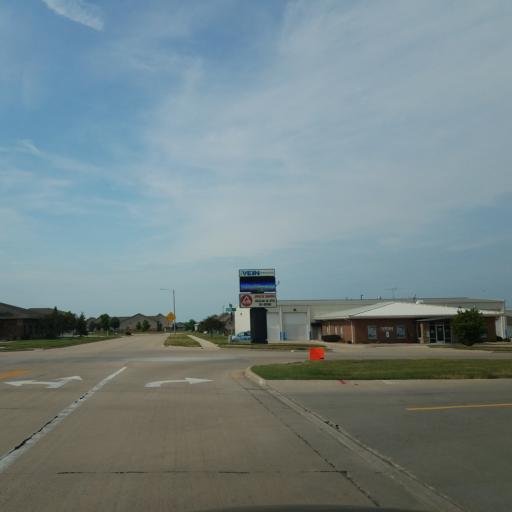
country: US
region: Illinois
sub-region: McLean County
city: Bloomington
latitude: 40.4890
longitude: -88.9098
